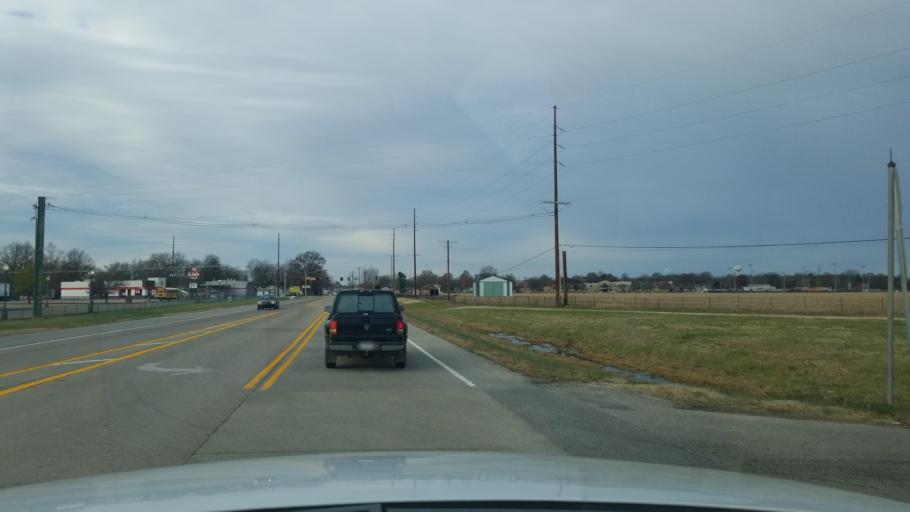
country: US
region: Indiana
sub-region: Posey County
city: Mount Vernon
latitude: 37.9373
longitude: -87.8762
